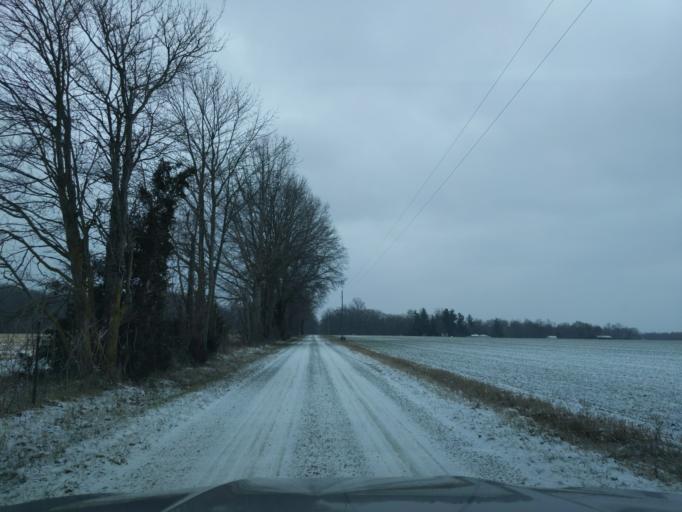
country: US
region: Indiana
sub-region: Decatur County
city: Westport
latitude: 39.2044
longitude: -85.4570
